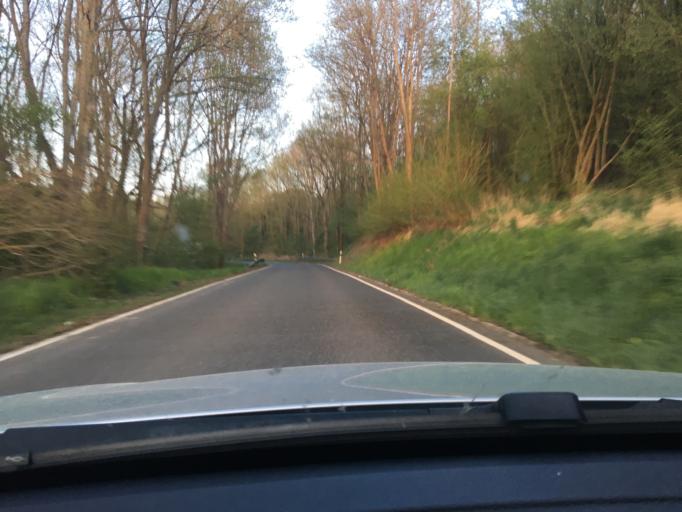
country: DE
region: Rheinland-Pfalz
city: Oberndorf
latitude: 49.7260
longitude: 7.8230
